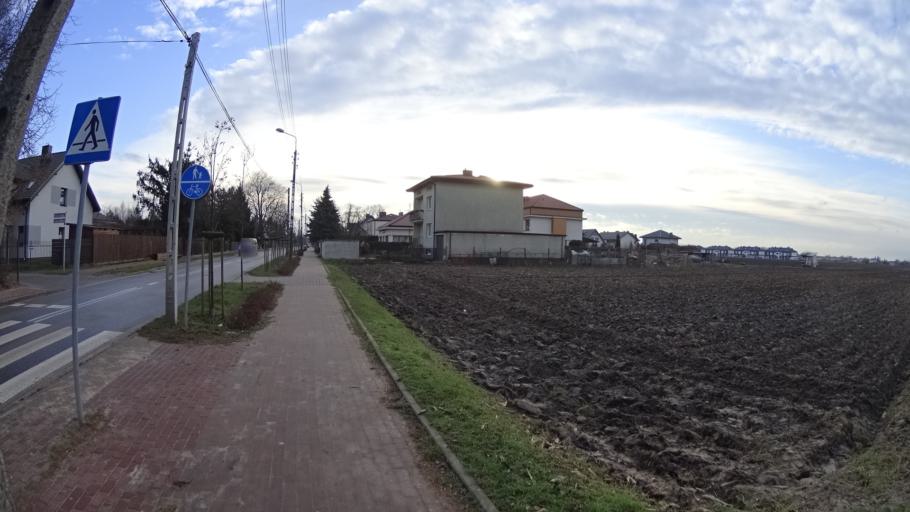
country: PL
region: Masovian Voivodeship
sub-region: Powiat warszawski zachodni
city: Ozarow Mazowiecki
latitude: 52.2235
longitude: 20.8012
